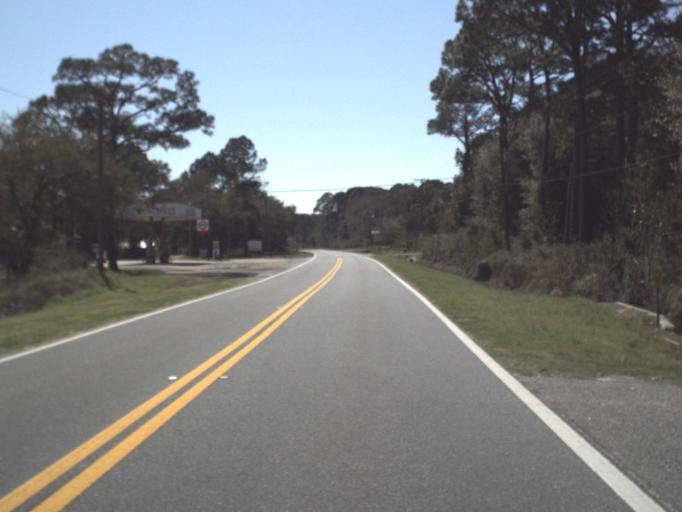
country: US
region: Florida
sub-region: Franklin County
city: Carrabelle
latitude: 29.8812
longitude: -84.5953
